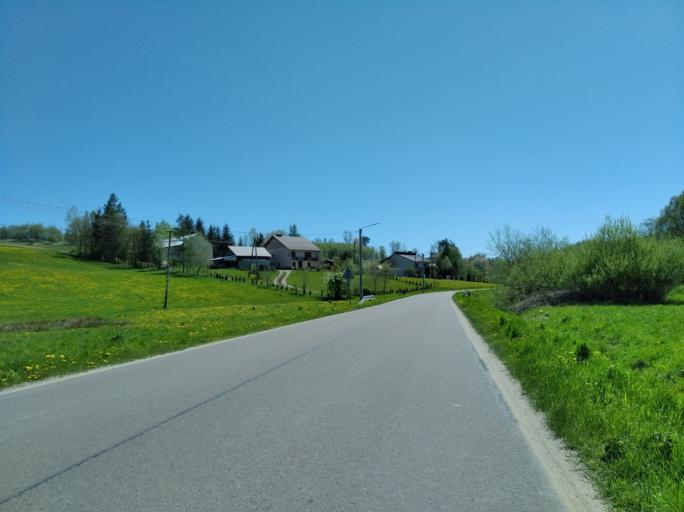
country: PL
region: Subcarpathian Voivodeship
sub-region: Powiat debicki
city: Brzostek
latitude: 49.9216
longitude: 21.4023
